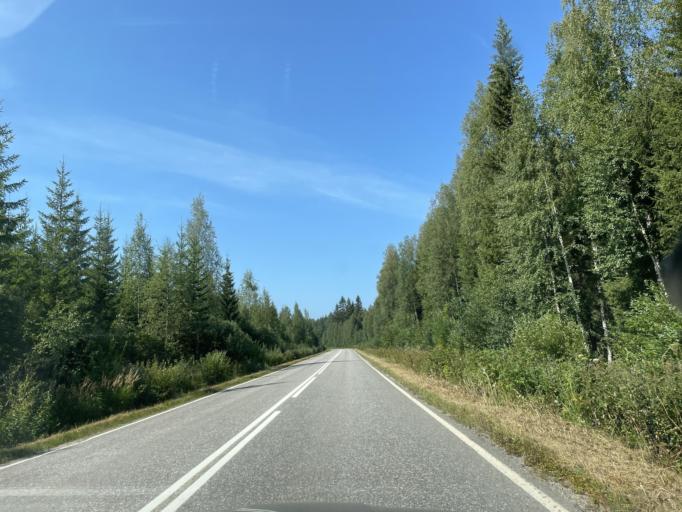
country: FI
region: Central Finland
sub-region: Saarijaervi-Viitasaari
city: Pihtipudas
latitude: 63.3676
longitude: 25.6872
